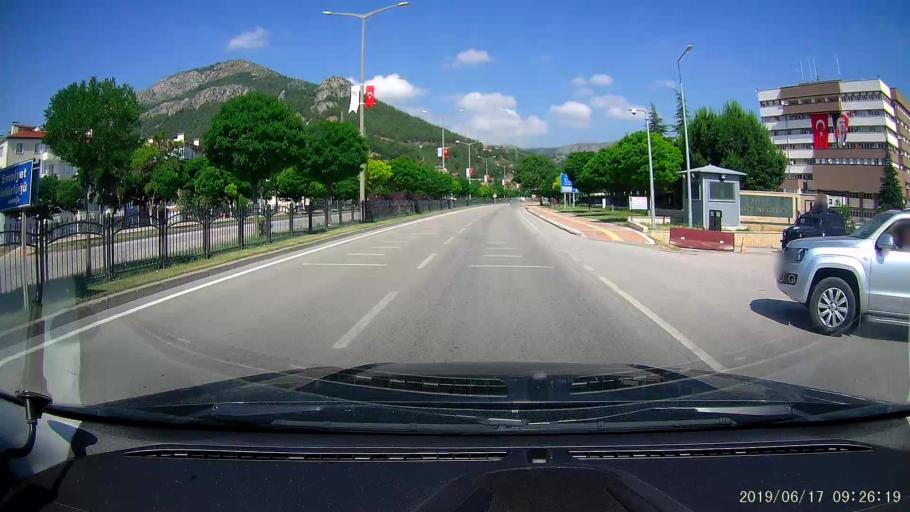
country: TR
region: Amasya
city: Amasya
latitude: 40.6690
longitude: 35.8373
